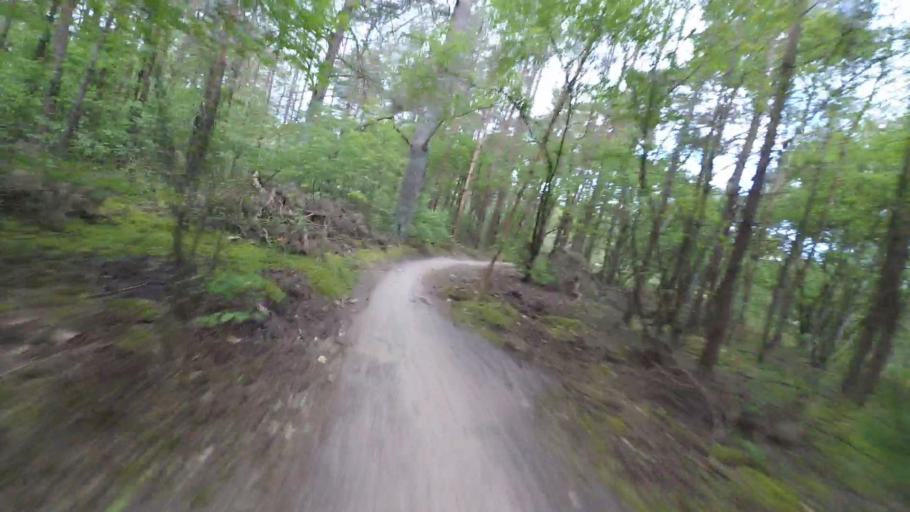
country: NL
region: Utrecht
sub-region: Gemeente Utrechtse Heuvelrug
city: Driebergen-Rijsenburg
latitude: 52.0824
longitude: 5.2744
